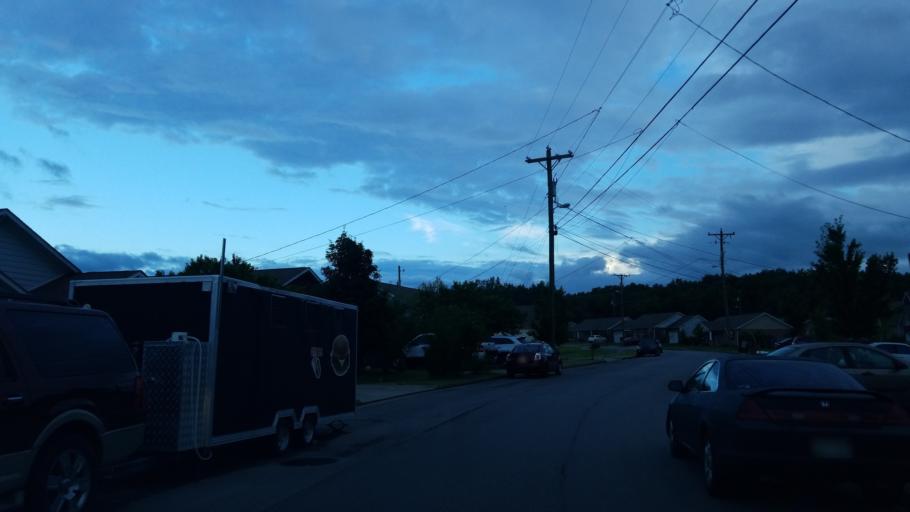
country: US
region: Tennessee
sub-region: Rutherford County
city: La Vergne
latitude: 36.0523
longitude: -86.5944
